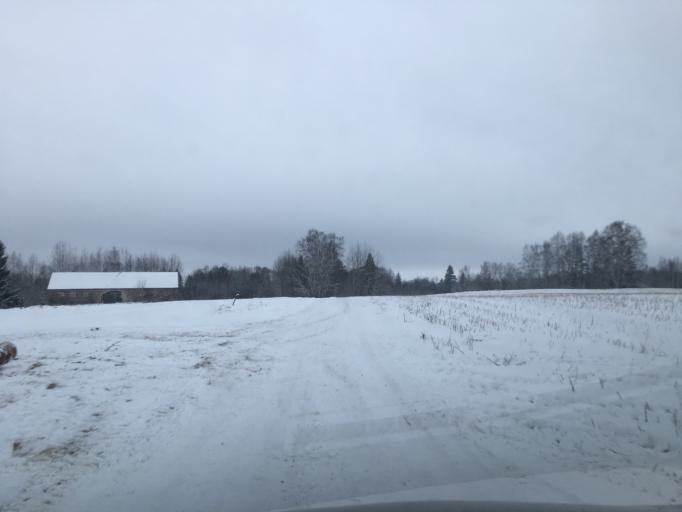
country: EE
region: Tartu
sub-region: Puhja vald
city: Puhja
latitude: 58.1925
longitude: 26.2020
